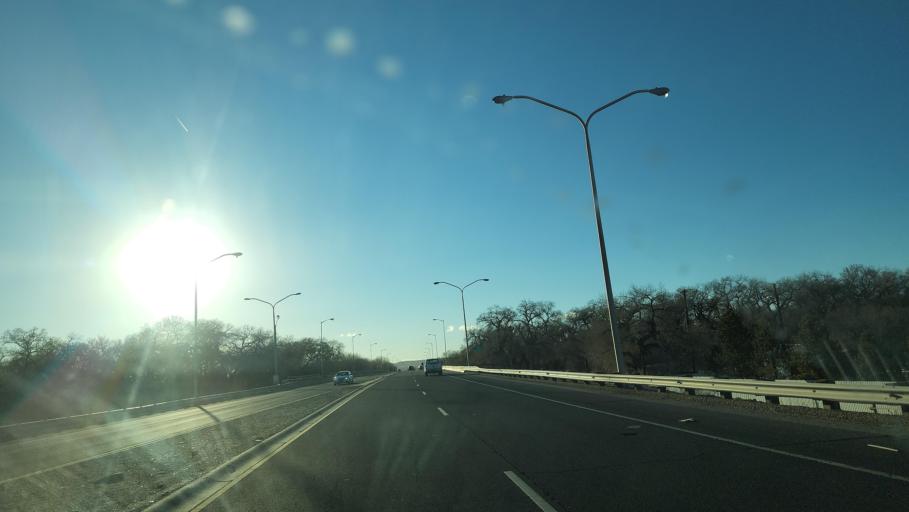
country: US
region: New Mexico
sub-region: Bernalillo County
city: South Valley
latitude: 35.0272
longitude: -106.6680
